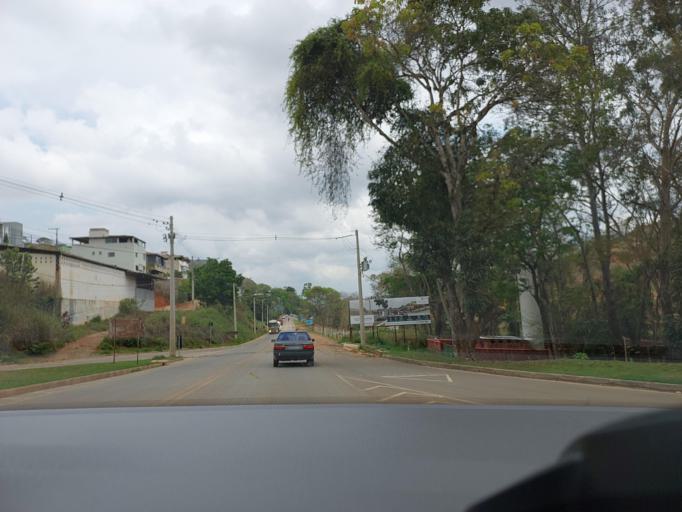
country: BR
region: Minas Gerais
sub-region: Ponte Nova
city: Ponte Nova
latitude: -20.3979
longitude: -42.8790
